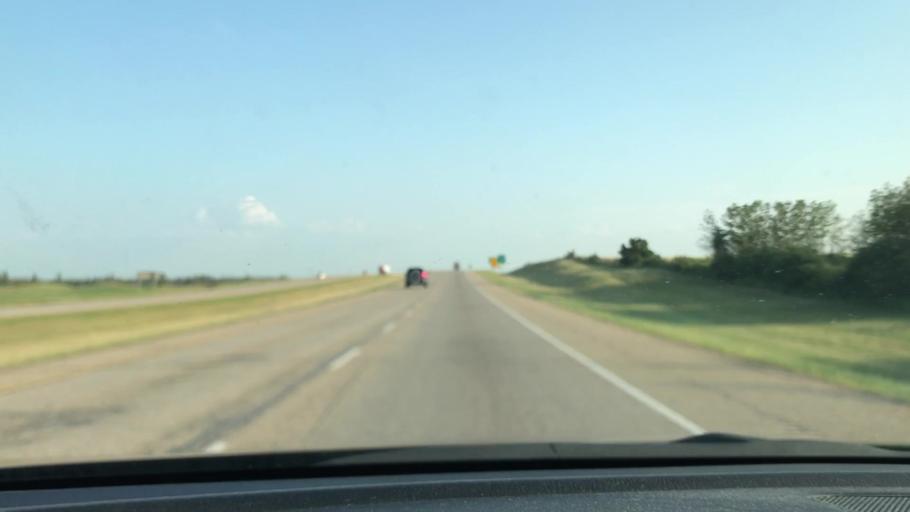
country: CA
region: Alberta
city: Ponoka
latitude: 52.5857
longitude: -113.6633
